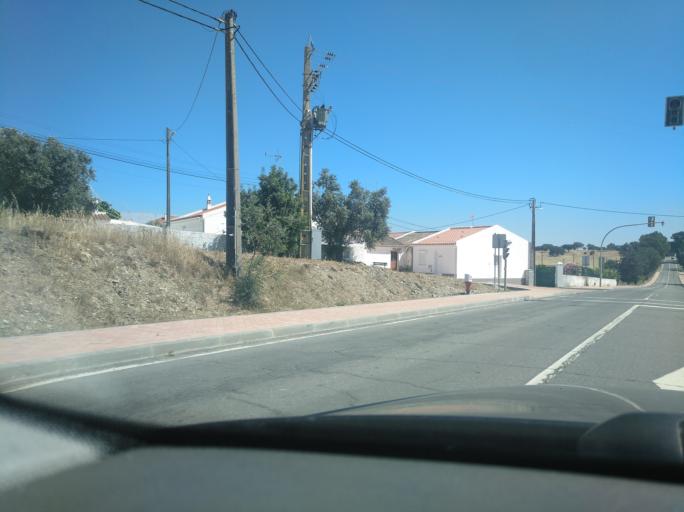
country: PT
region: Beja
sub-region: Almodovar
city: Almodovar
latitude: 37.6043
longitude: -8.0815
